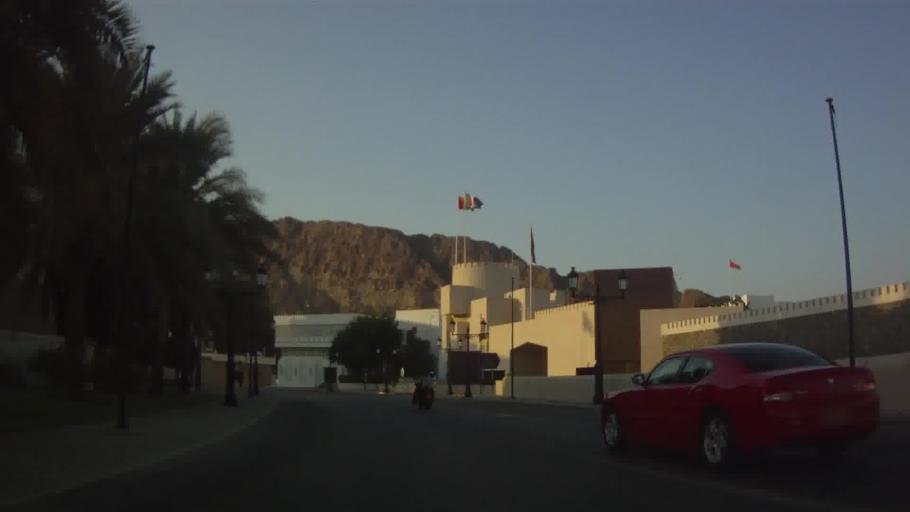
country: OM
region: Muhafazat Masqat
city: Muscat
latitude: 23.6145
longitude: 58.5910
